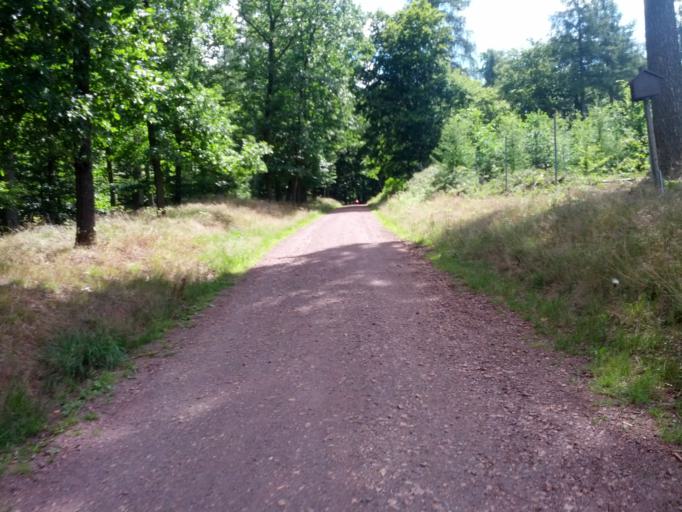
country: DE
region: Thuringia
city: Wolfsburg-Unkeroda
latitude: 50.9352
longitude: 10.3117
